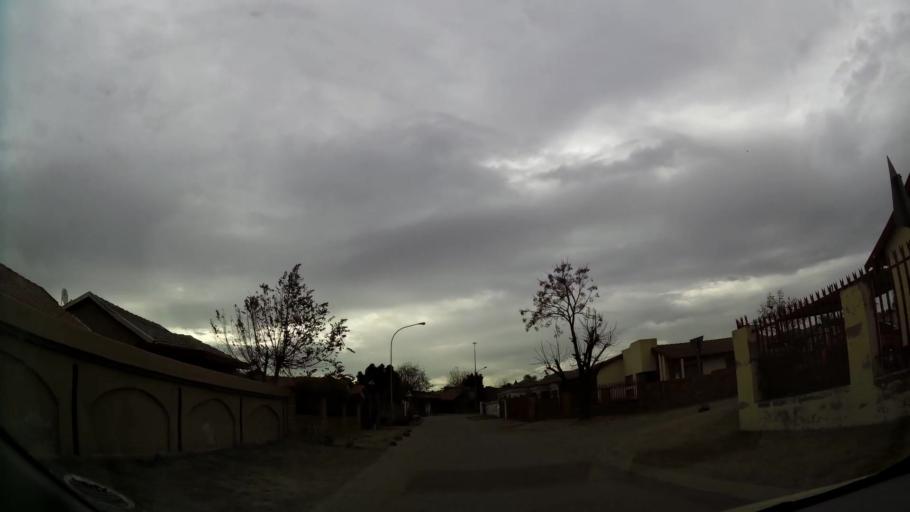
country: ZA
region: Gauteng
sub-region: City of Tshwane Metropolitan Municipality
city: Pretoria
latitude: -25.7117
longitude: 28.3284
